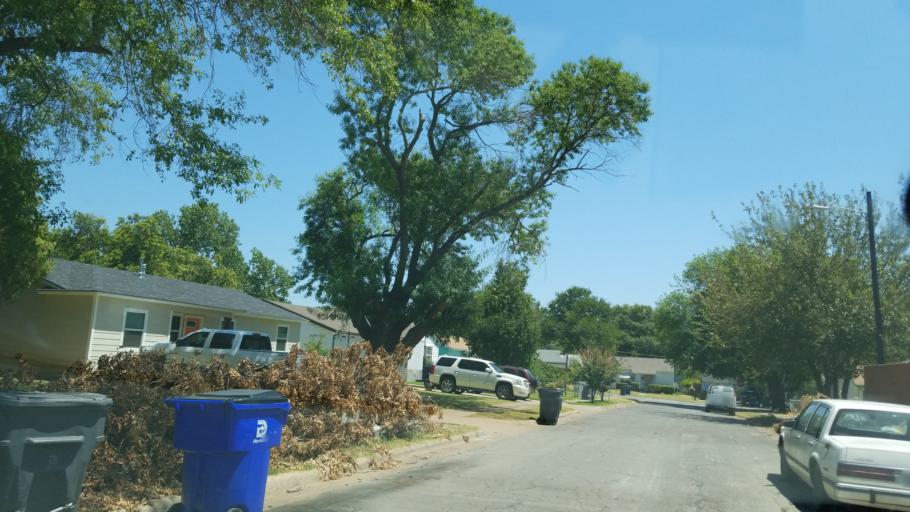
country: US
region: Texas
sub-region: Dallas County
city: Cockrell Hill
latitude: 32.7338
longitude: -96.8835
